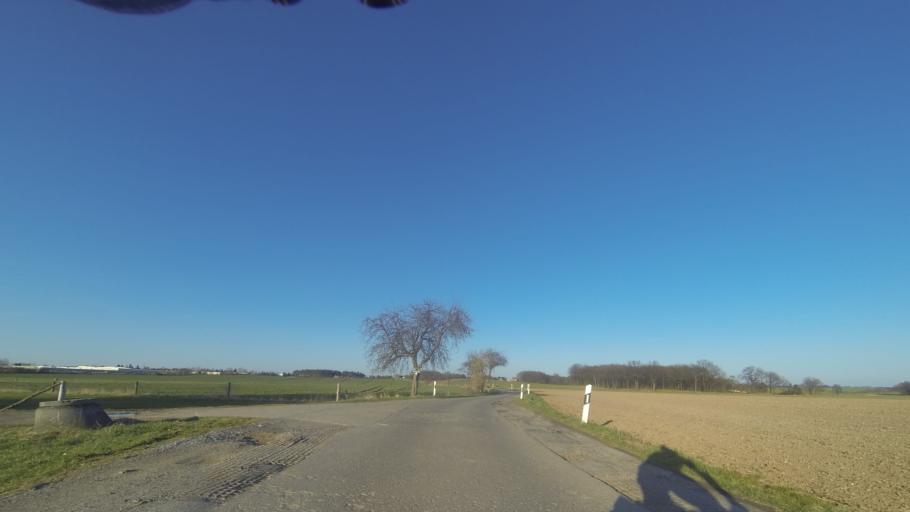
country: DE
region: Saxony
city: Ottendorf-Okrilla
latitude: 51.1748
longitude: 13.7778
